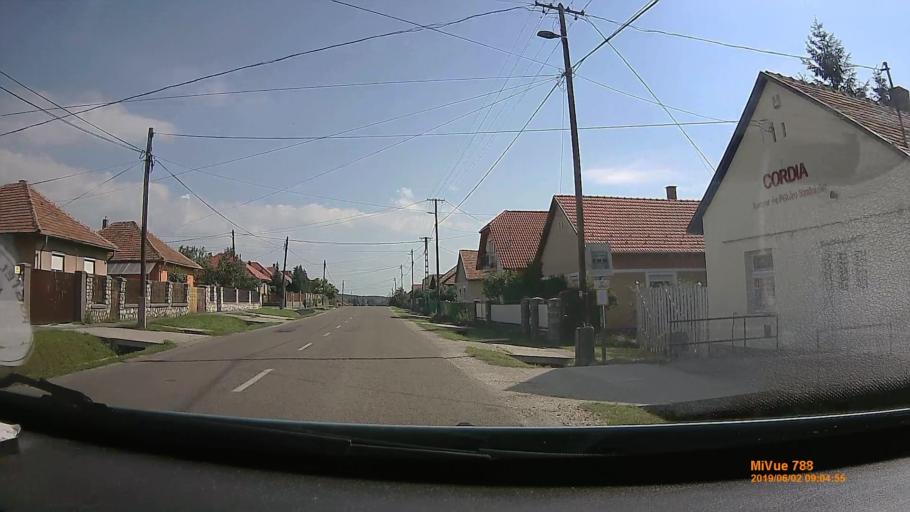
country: HU
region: Borsod-Abauj-Zemplen
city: Kazincbarcika
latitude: 48.1740
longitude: 20.6457
